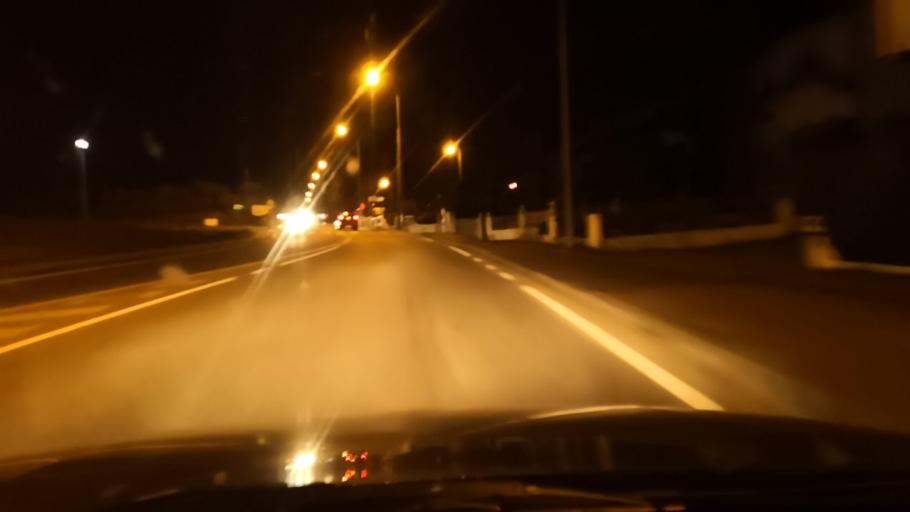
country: PT
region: Castelo Branco
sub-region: Concelho do Fundao
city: Fundao
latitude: 40.1597
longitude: -7.4981
